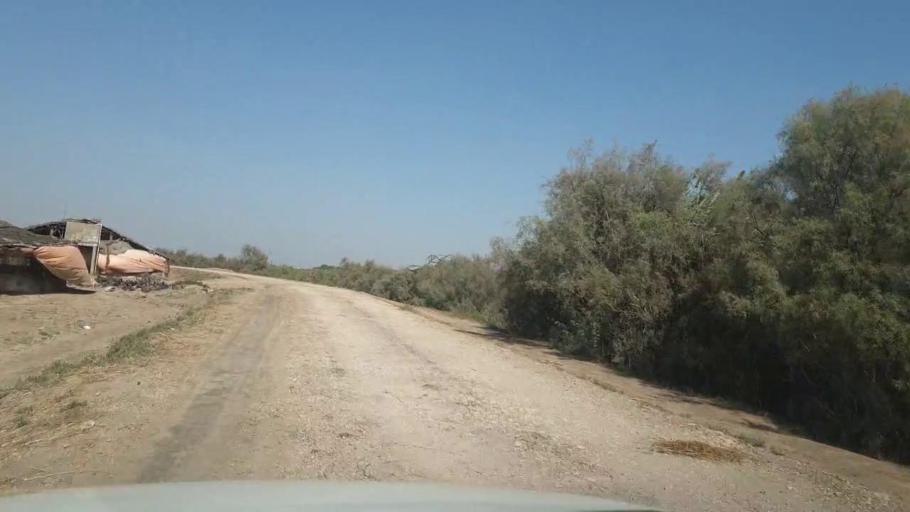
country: PK
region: Sindh
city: Chuhar Jamali
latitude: 24.3799
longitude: 67.8022
